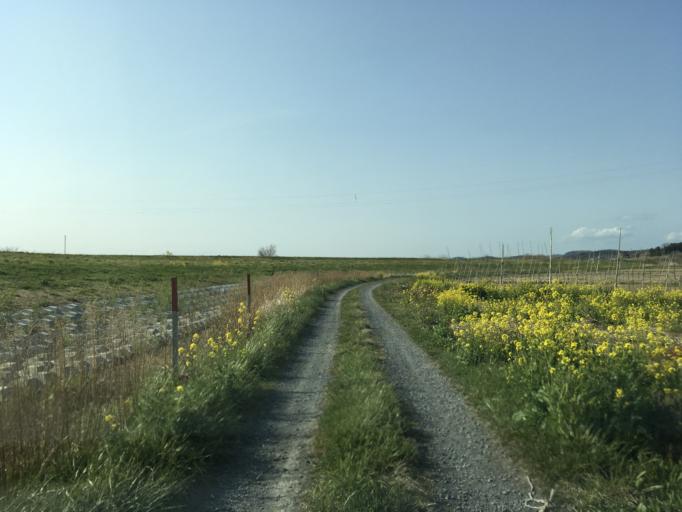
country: JP
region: Miyagi
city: Wakuya
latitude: 38.7136
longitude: 141.2699
